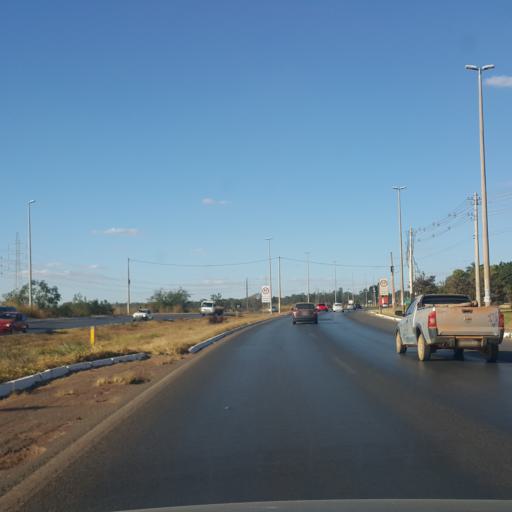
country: BR
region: Federal District
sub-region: Brasilia
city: Brasilia
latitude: -15.7990
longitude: -48.0748
